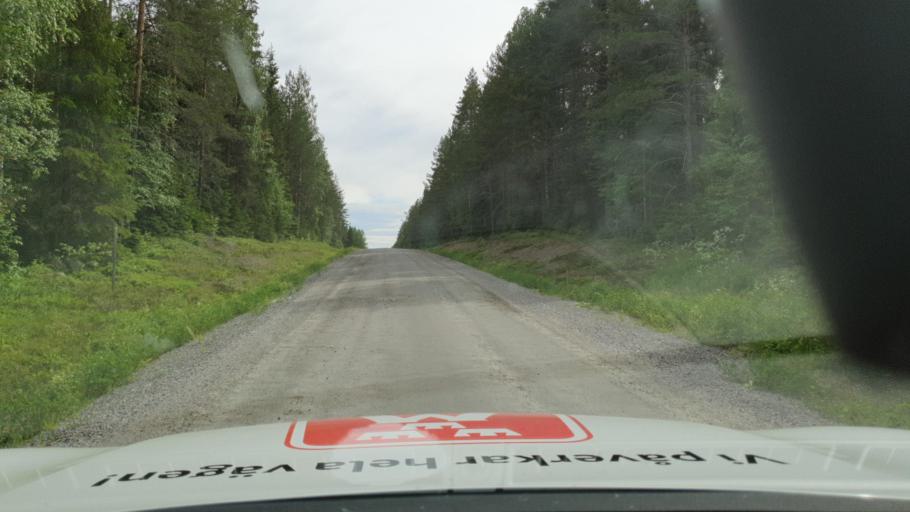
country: SE
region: Vaesterbotten
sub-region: Skelleftea Kommun
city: Burea
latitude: 64.4399
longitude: 21.0171
